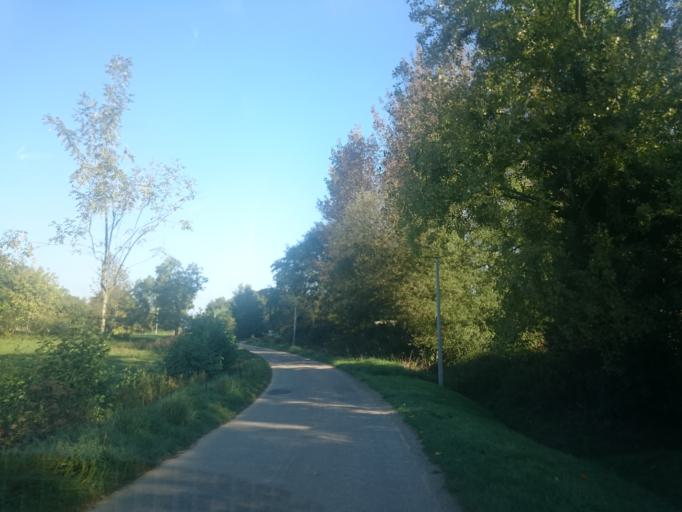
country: FR
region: Brittany
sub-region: Departement d'Ille-et-Vilaine
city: Tresboeuf
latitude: 47.9282
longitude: -1.5654
